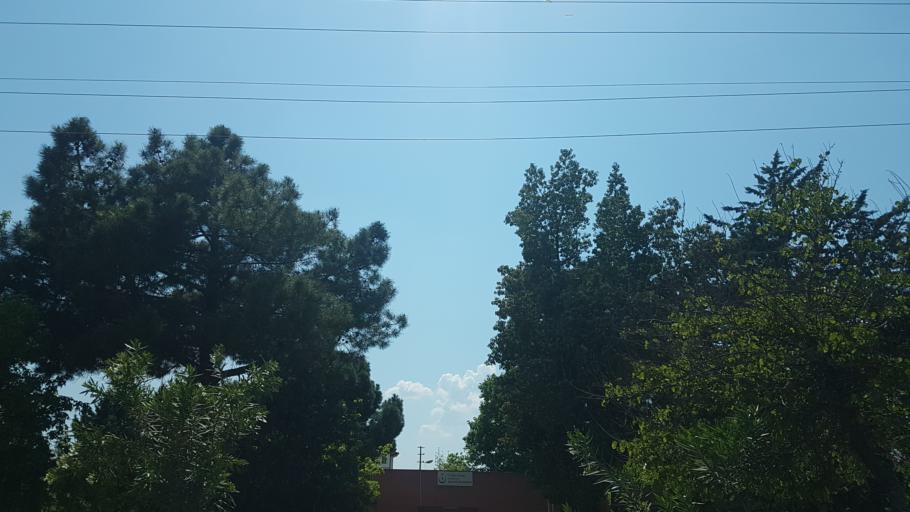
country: TR
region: Adana
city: Adana
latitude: 37.0205
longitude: 35.3721
